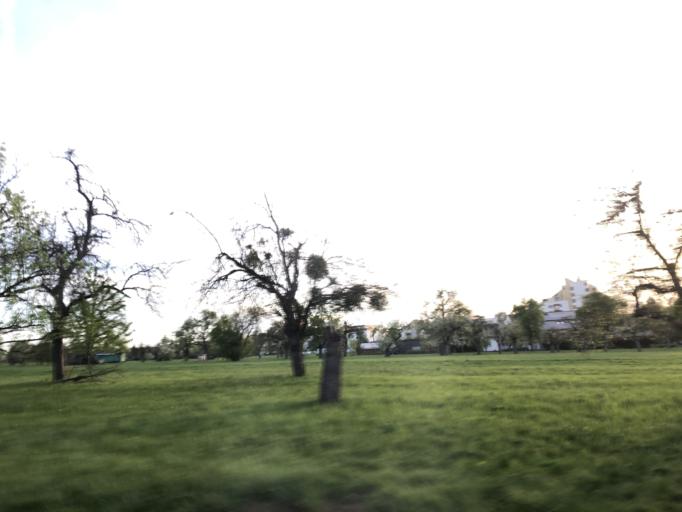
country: DE
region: Baden-Wuerttemberg
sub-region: Regierungsbezirk Stuttgart
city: Filderstadt
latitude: 48.6720
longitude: 9.2206
